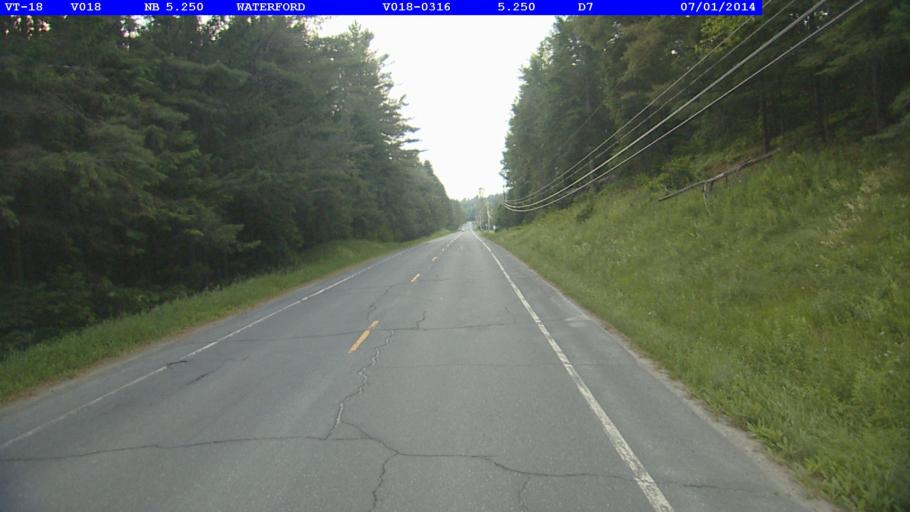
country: US
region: Vermont
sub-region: Caledonia County
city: Saint Johnsbury
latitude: 44.4065
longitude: -71.9270
